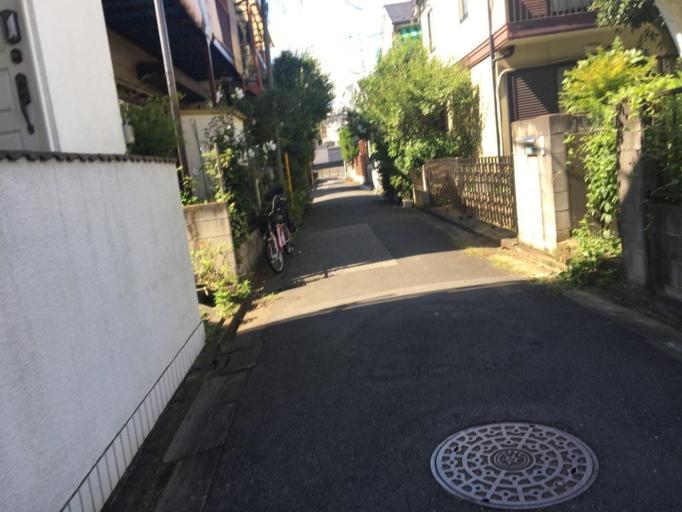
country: JP
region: Chiba
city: Matsudo
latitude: 35.7345
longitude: 139.8469
